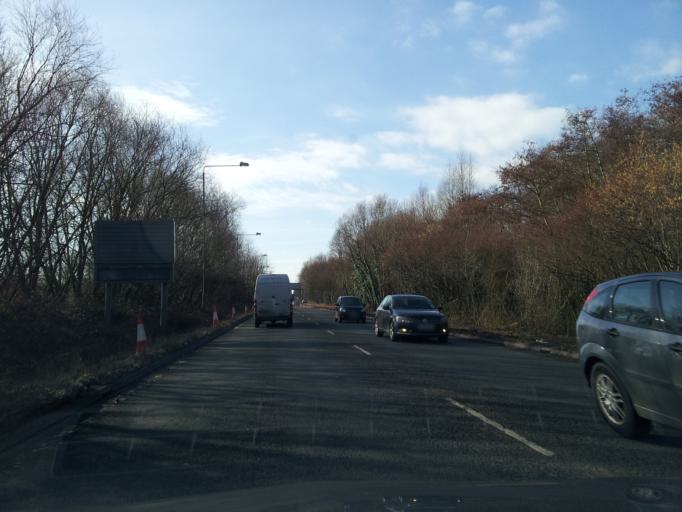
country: GB
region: England
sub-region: Nottinghamshire
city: West Bridgford
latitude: 52.9056
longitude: -1.1107
